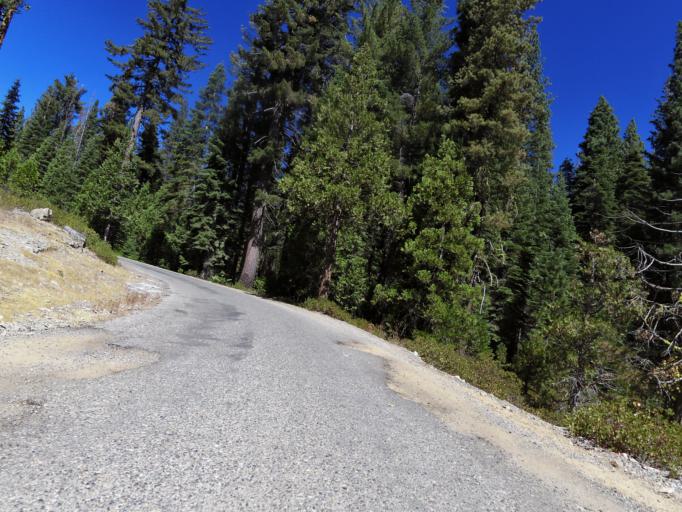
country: US
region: California
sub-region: Madera County
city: Oakhurst
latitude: 37.4376
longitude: -119.5409
